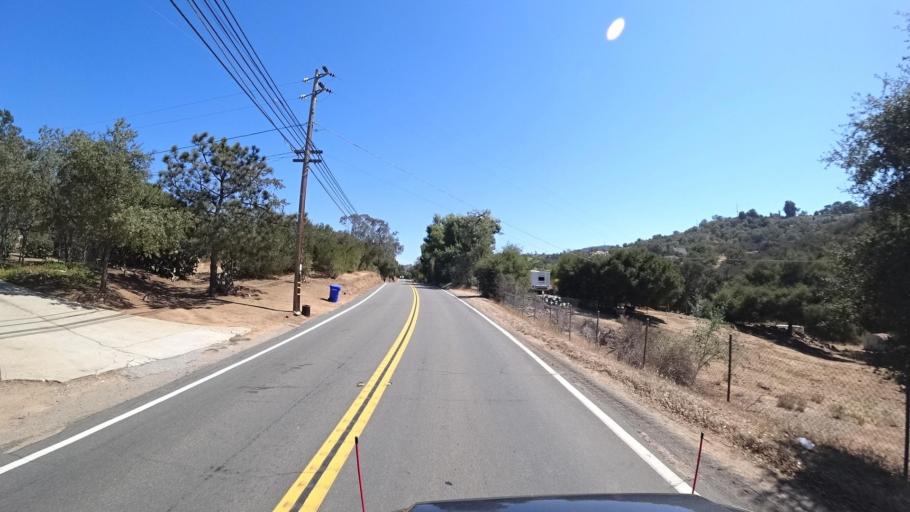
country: US
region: California
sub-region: San Diego County
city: Hidden Meadows
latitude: 33.2684
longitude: -117.0794
